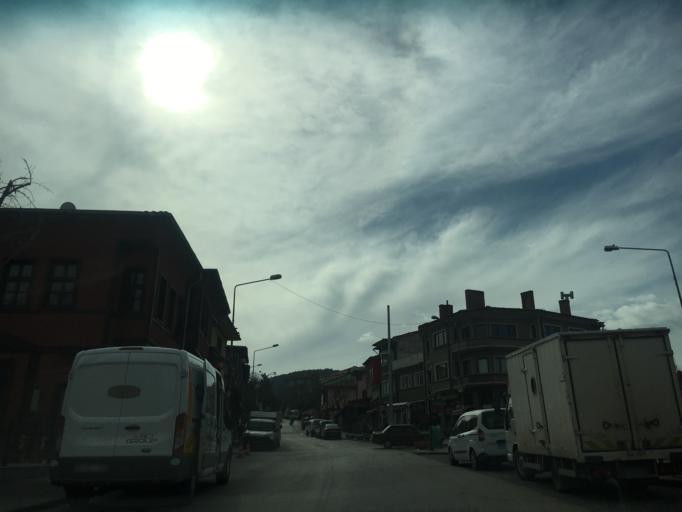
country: TR
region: Eskisehir
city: Eskisehir
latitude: 39.7646
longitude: 30.5241
